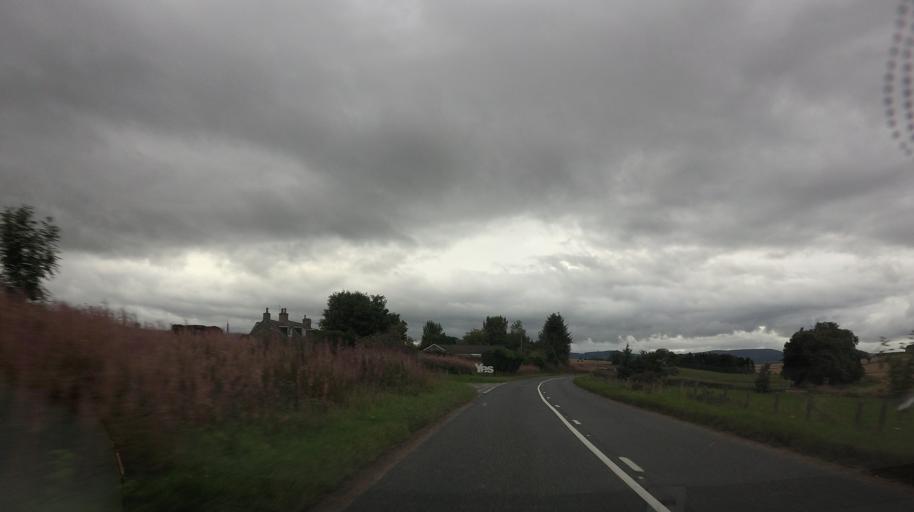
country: GB
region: Scotland
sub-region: Aberdeenshire
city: Kemnay
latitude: 57.1806
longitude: -2.4667
